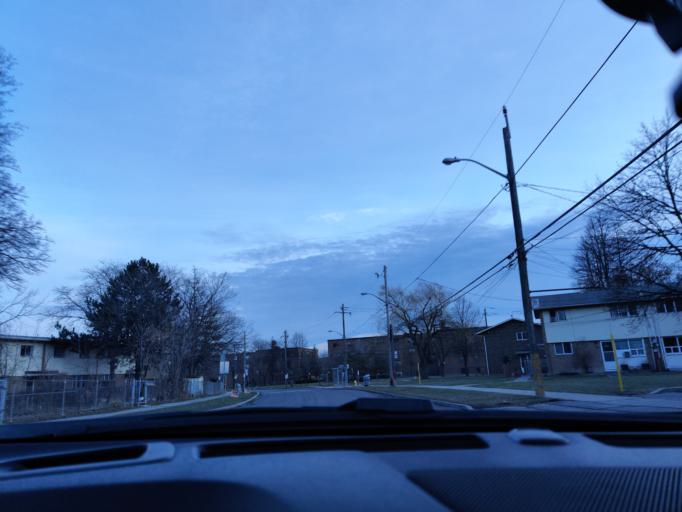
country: CA
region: Ontario
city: Toronto
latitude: 43.7198
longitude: -79.4489
